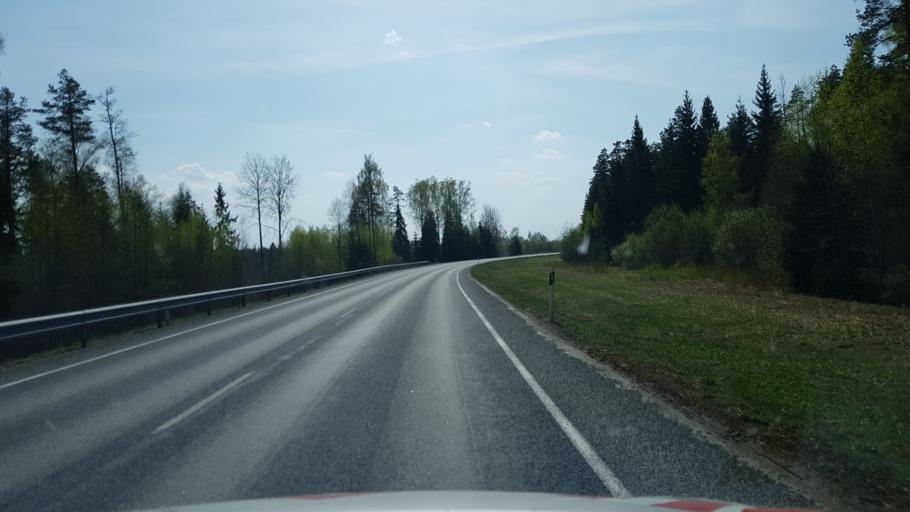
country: EE
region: Jaervamaa
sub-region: Tueri vald
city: Sarevere
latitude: 58.7376
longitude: 25.3003
